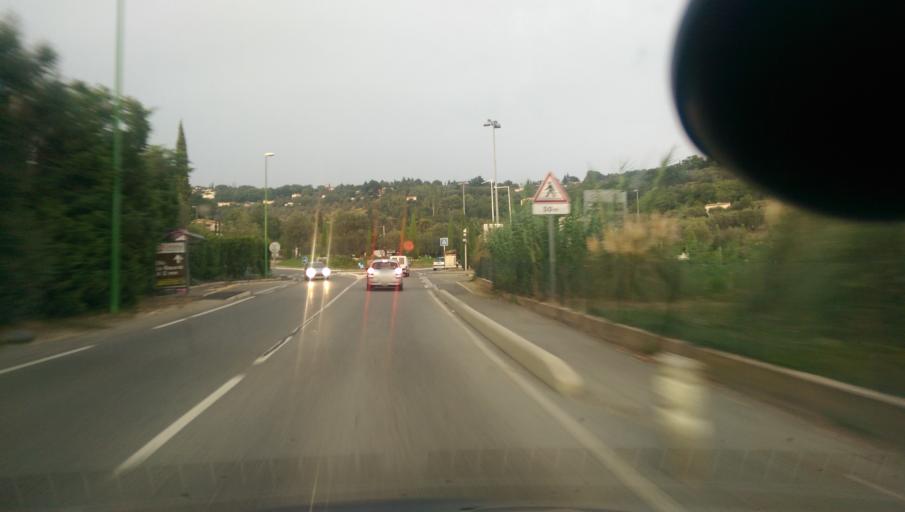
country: FR
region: Provence-Alpes-Cote d'Azur
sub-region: Departement des Alpes-Maritimes
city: Chateauneuf-Grasse
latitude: 43.6673
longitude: 6.9846
